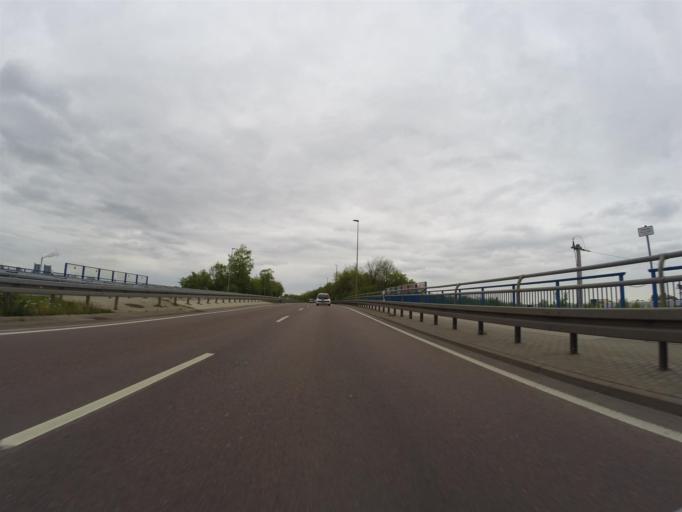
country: DE
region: Saxony-Anhalt
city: Merseburg
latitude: 51.3757
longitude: 11.9819
